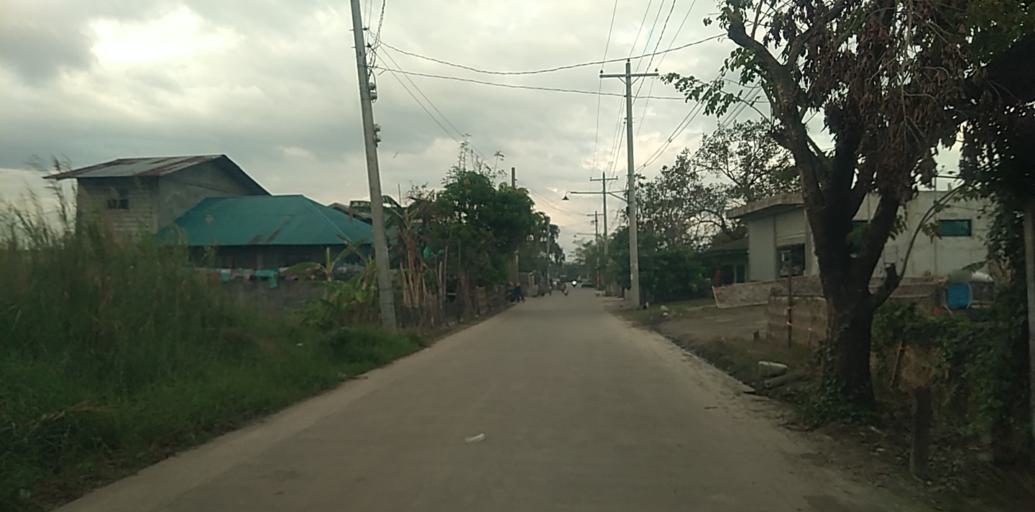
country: PH
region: Central Luzon
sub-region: Province of Pampanga
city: San Fernando
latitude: 15.0082
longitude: 120.7036
